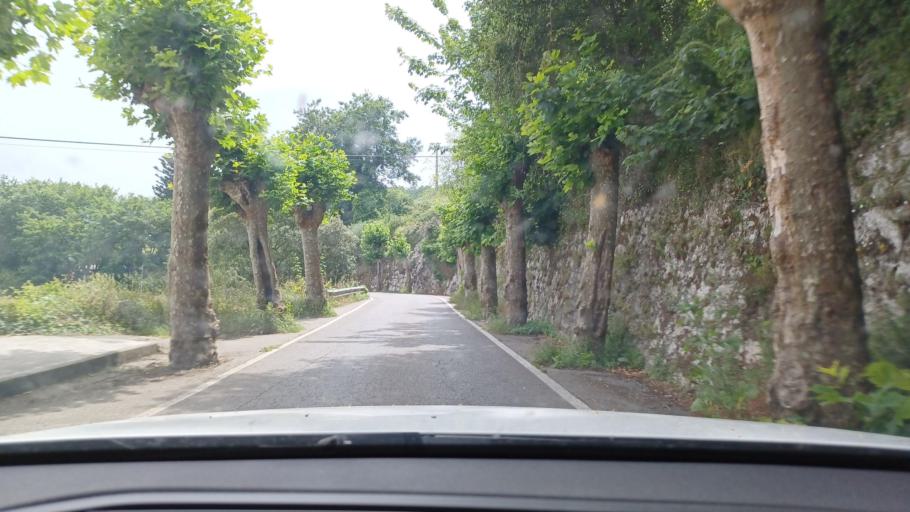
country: ES
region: Asturias
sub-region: Province of Asturias
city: Llanes
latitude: 43.4194
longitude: -4.7572
